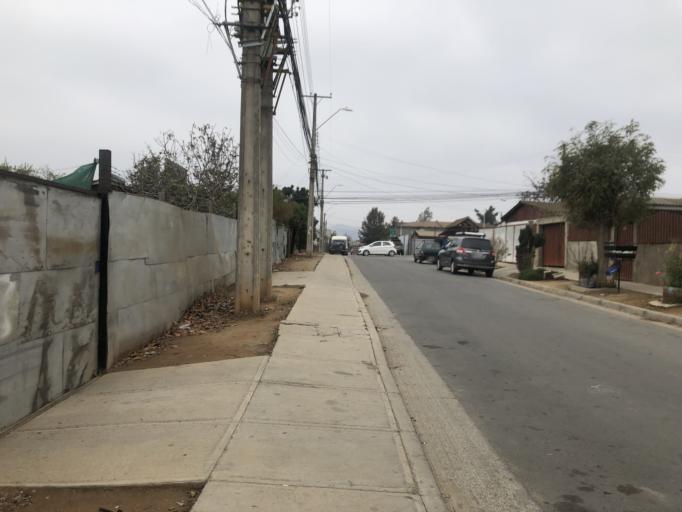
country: CL
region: Valparaiso
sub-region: Provincia de Marga Marga
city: Quilpue
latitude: -33.0492
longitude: -71.4267
